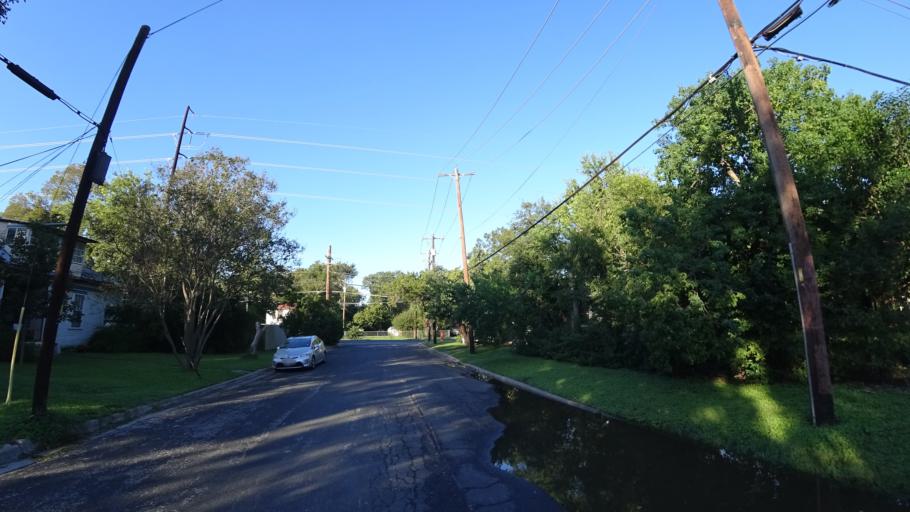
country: US
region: Texas
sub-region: Travis County
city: Austin
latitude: 30.2993
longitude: -97.7324
